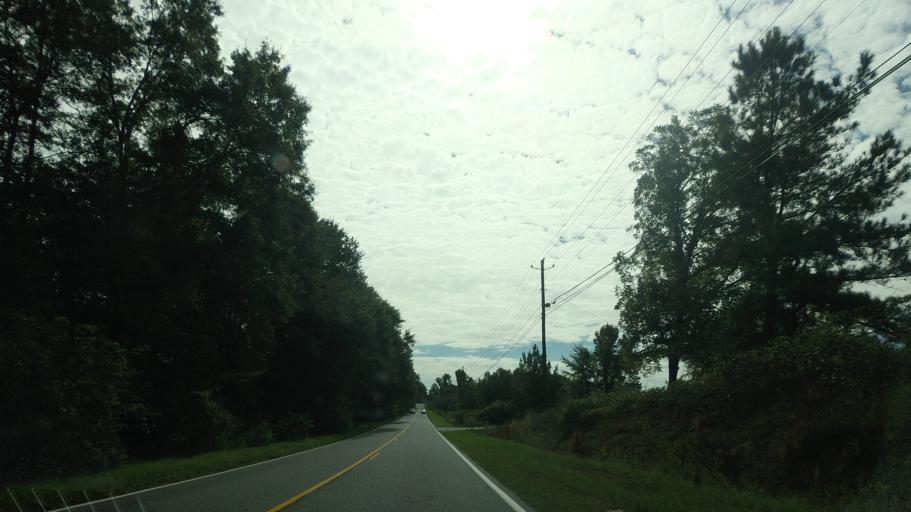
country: US
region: Georgia
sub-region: Houston County
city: Centerville
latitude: 32.7002
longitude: -83.7047
